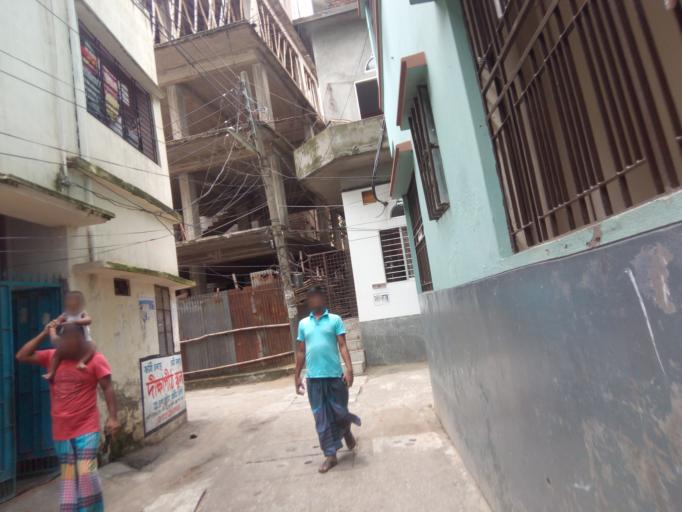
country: BD
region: Dhaka
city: Azimpur
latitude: 23.7468
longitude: 90.3674
